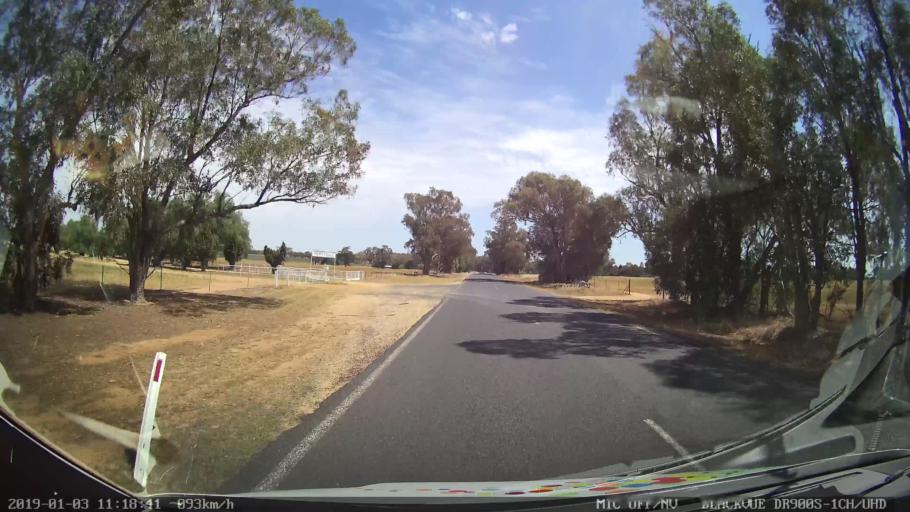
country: AU
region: New South Wales
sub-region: Young
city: Young
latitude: -34.1227
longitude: 148.2614
